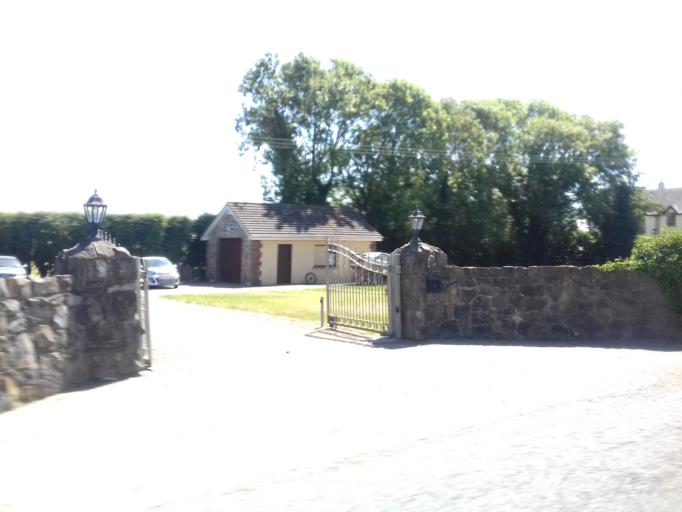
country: IE
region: Leinster
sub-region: Fingal County
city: Swords
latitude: 53.4999
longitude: -6.2698
